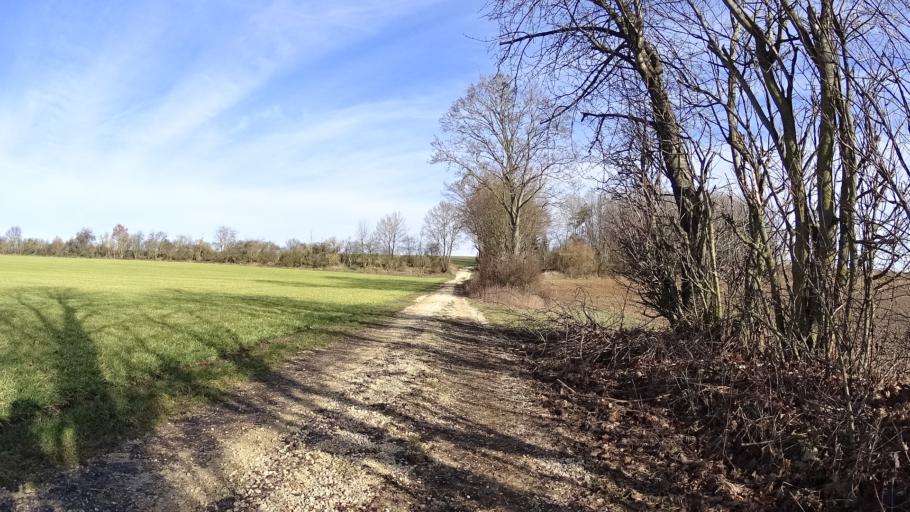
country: DE
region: Bavaria
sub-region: Upper Bavaria
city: Hitzhofen
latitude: 48.8354
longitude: 11.3415
